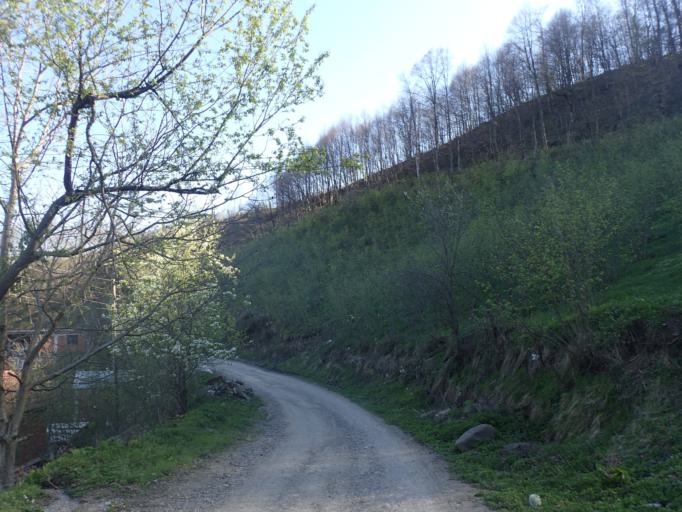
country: TR
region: Ordu
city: Korgan
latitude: 40.7542
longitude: 37.3089
